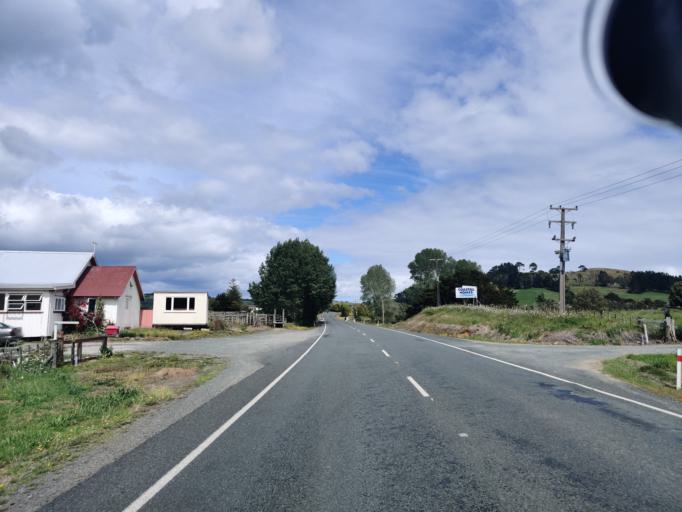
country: NZ
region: Northland
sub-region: Far North District
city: Taipa
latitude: -35.0027
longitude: 173.6012
